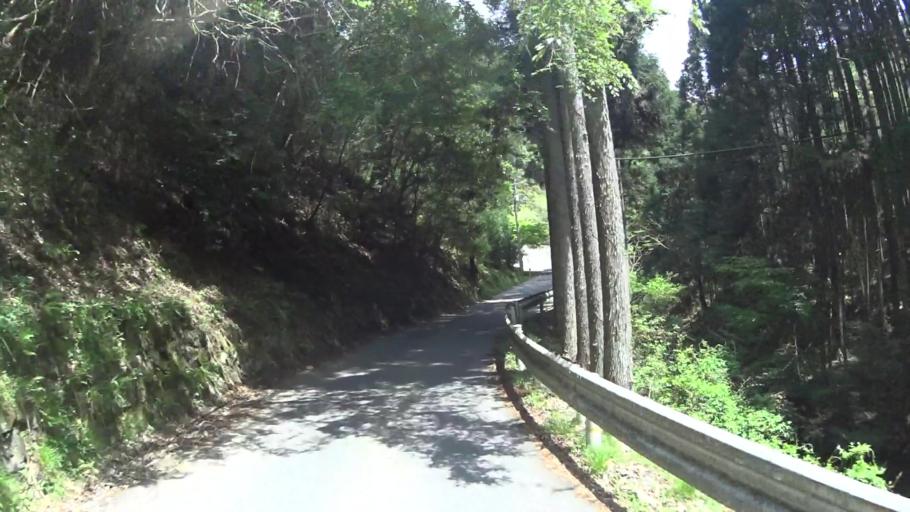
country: JP
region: Kyoto
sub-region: Kyoto-shi
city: Kamigyo-ku
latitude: 35.1099
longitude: 135.7036
